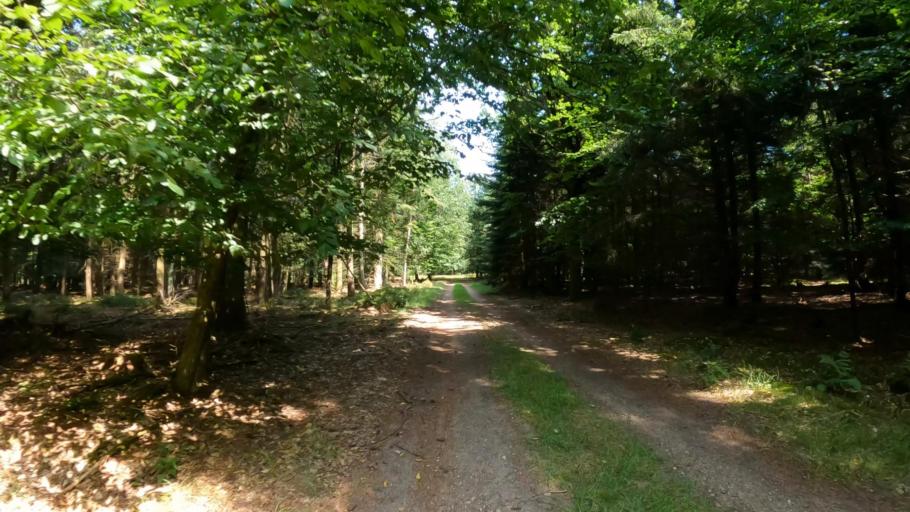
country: DE
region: Schleswig-Holstein
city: Bark
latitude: 53.9333
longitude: 10.1909
